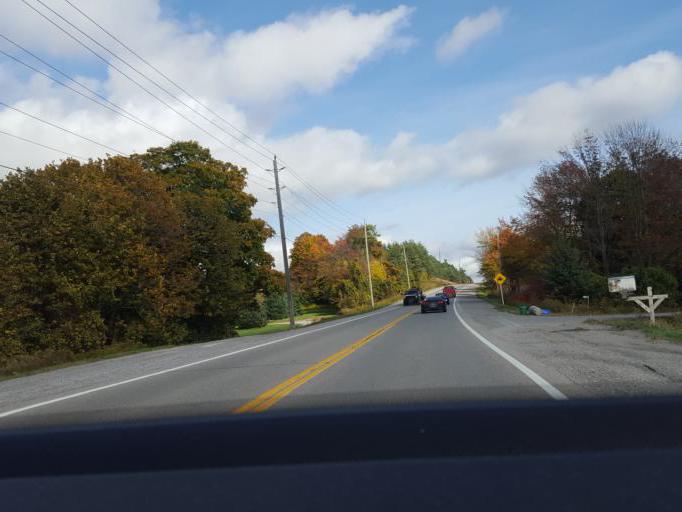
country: CA
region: Ontario
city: Oshawa
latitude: 43.9817
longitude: -78.6684
